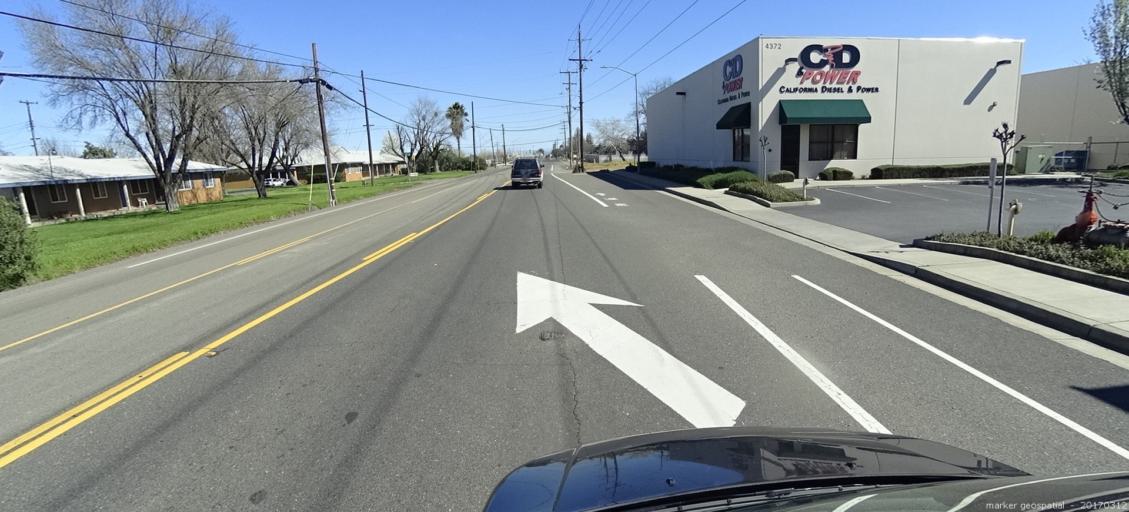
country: US
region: California
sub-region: Sacramento County
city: Rio Linda
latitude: 38.6472
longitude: -121.4196
